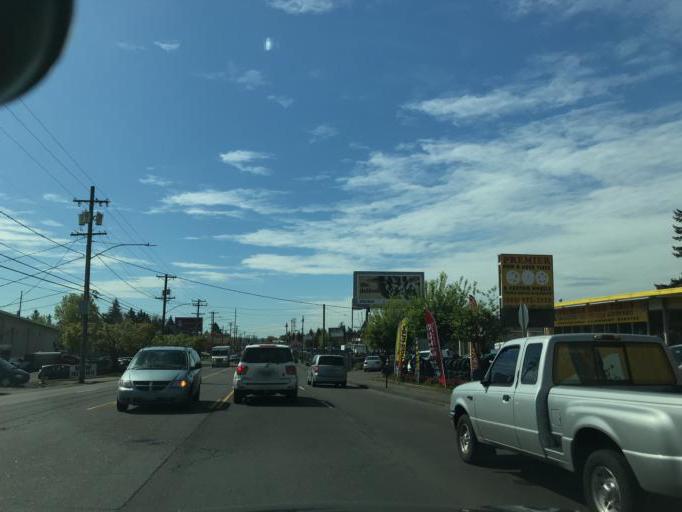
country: US
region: Oregon
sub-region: Multnomah County
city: Lents
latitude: 45.4670
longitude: -122.5791
